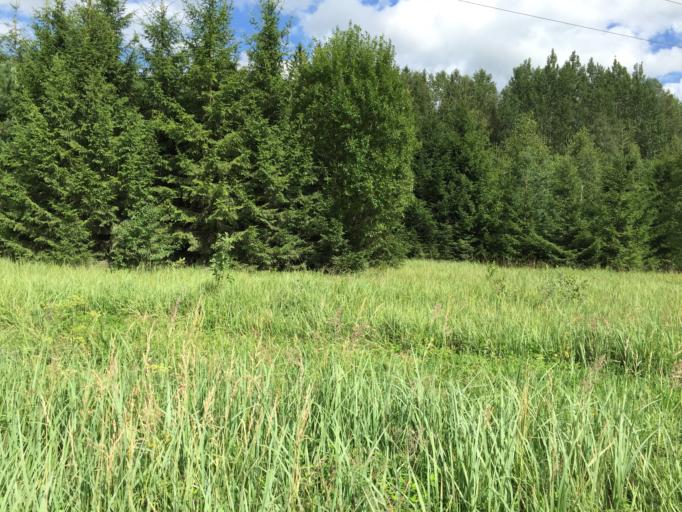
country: LV
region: Malpils
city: Malpils
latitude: 56.8692
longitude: 25.0086
